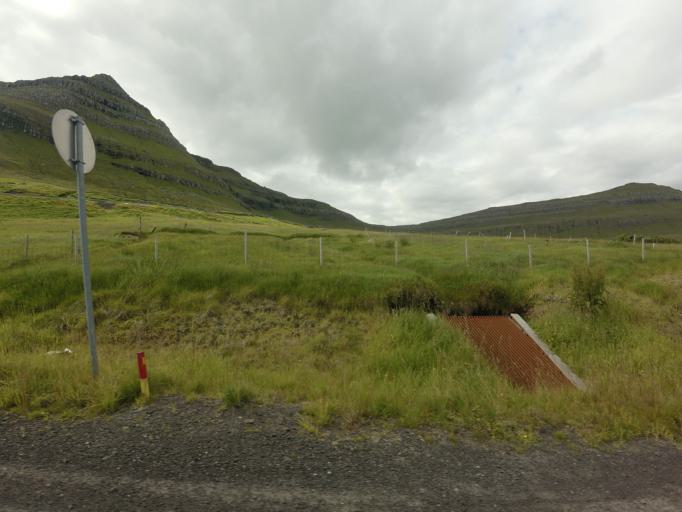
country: FO
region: Eysturoy
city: Eystur
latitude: 62.2091
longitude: -6.6955
